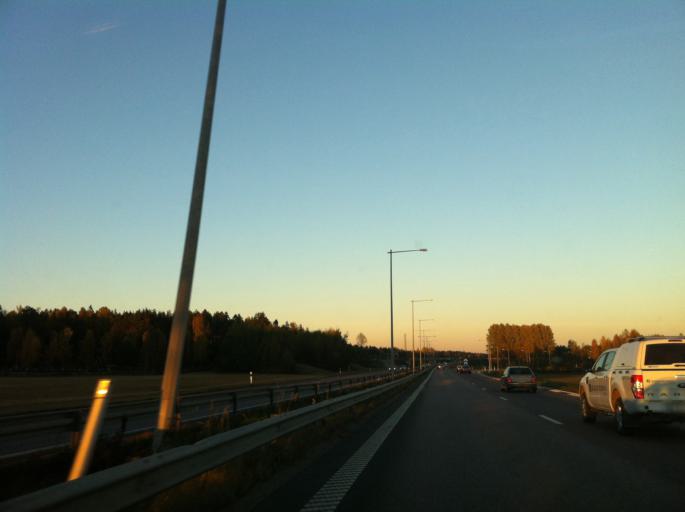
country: SE
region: Gaevleborg
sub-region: Gavle Kommun
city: Valbo
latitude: 60.6634
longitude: 17.0714
